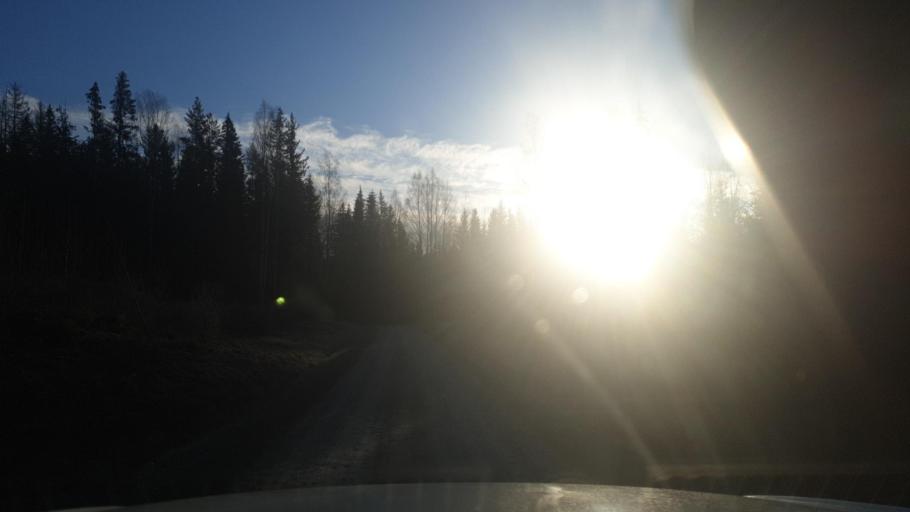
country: SE
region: Vaermland
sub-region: Sunne Kommun
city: Sunne
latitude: 59.6655
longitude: 13.0404
